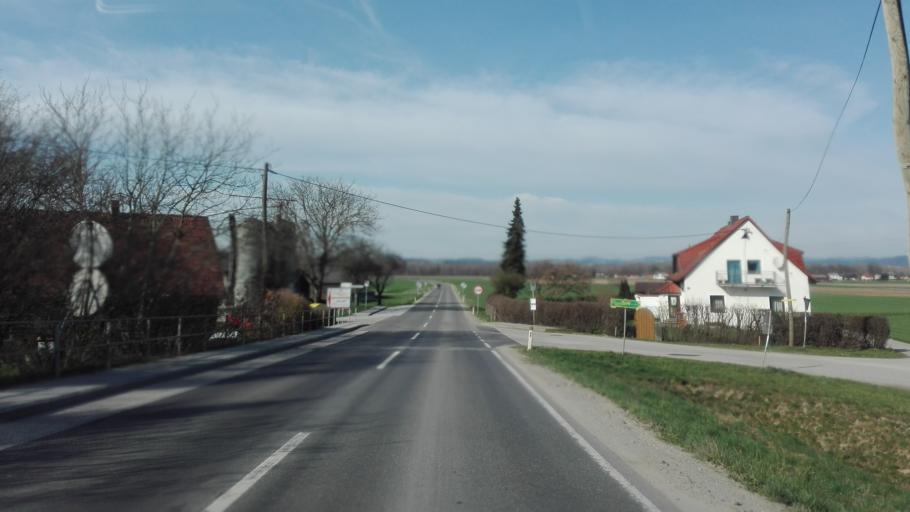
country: AT
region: Lower Austria
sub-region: Politischer Bezirk Amstetten
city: Ennsdorf
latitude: 48.2178
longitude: 14.5397
